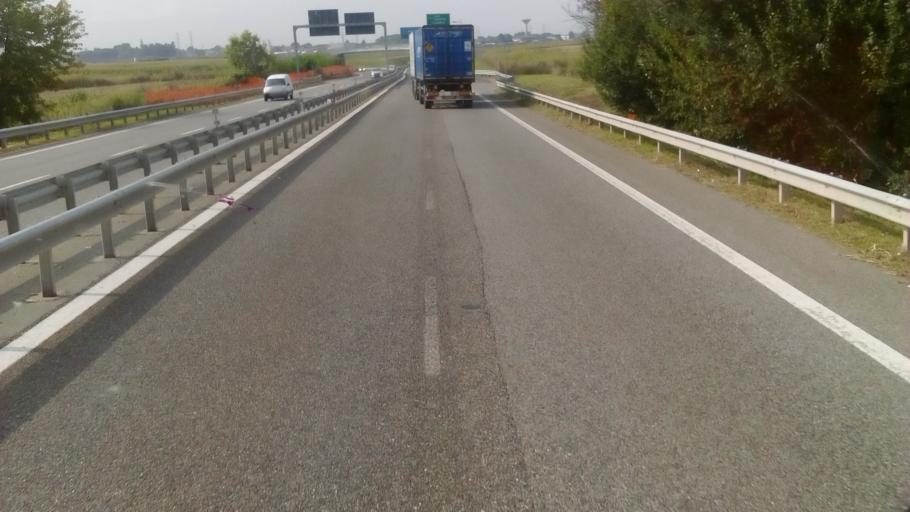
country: IT
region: Lombardy
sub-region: Provincia di Como
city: Cermenate
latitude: 45.6906
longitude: 9.0959
